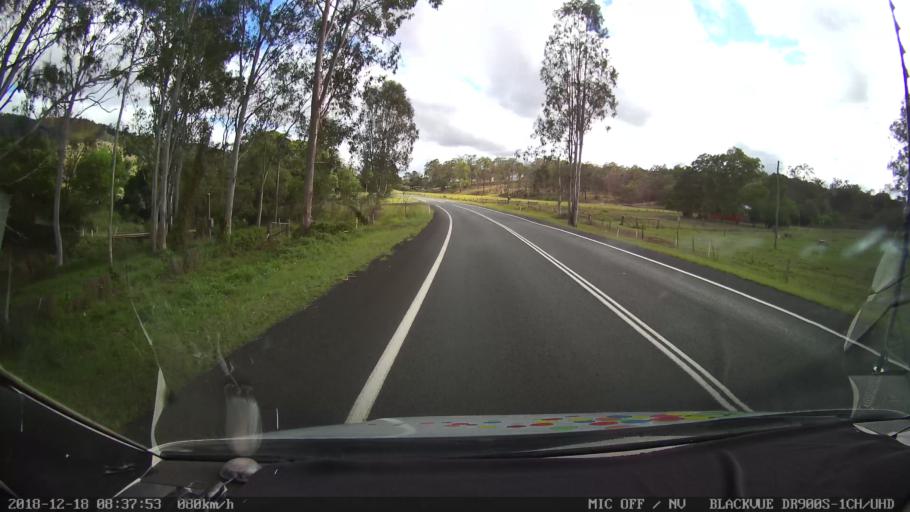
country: AU
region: New South Wales
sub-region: Kyogle
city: Kyogle
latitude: -28.2610
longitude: 152.8223
